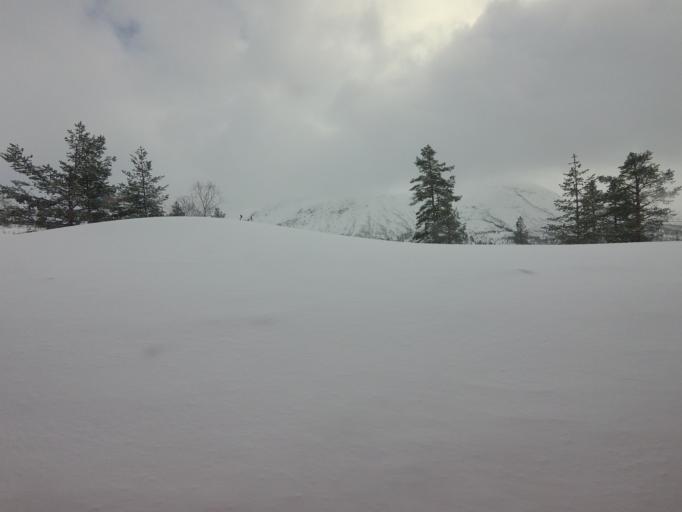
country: NO
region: Hordaland
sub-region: Ulvik
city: Ulvik
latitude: 60.7084
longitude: 6.8947
